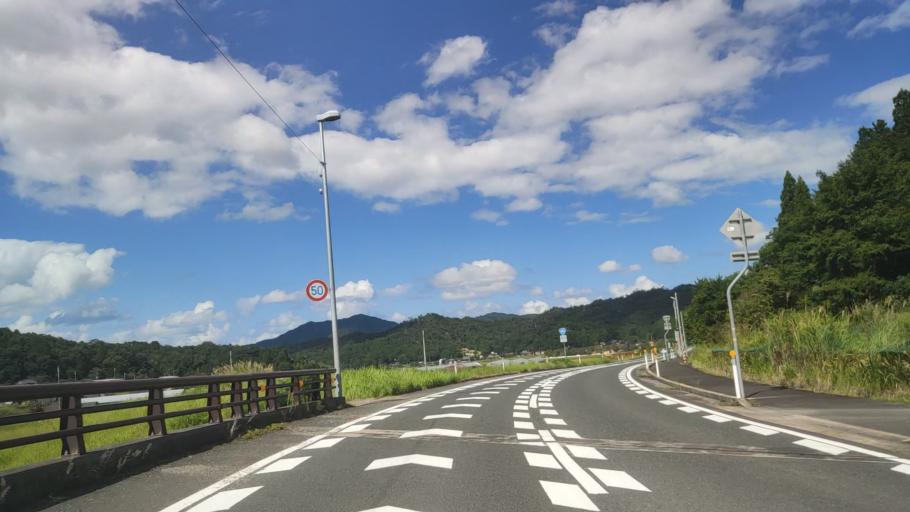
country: JP
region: Hyogo
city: Toyooka
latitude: 35.5665
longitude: 134.9737
